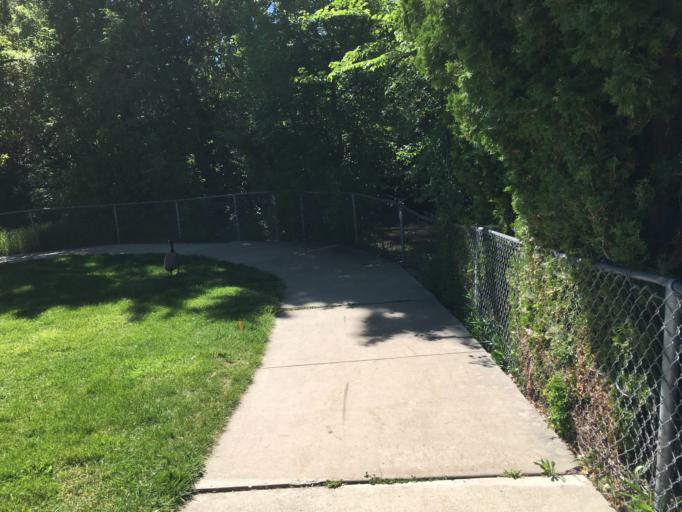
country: US
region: Utah
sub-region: Davis County
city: Layton
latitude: 41.0670
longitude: -111.9632
